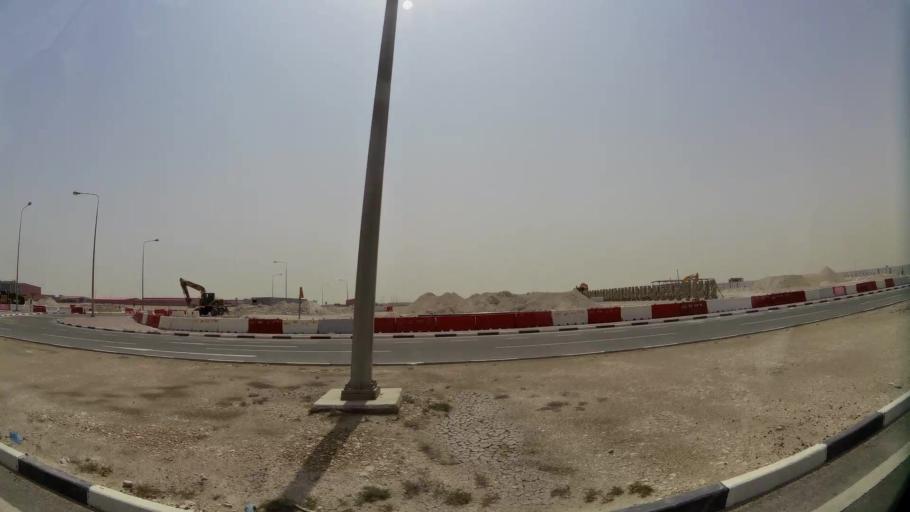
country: QA
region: Al Wakrah
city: Al Wukayr
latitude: 25.1476
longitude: 51.3949
